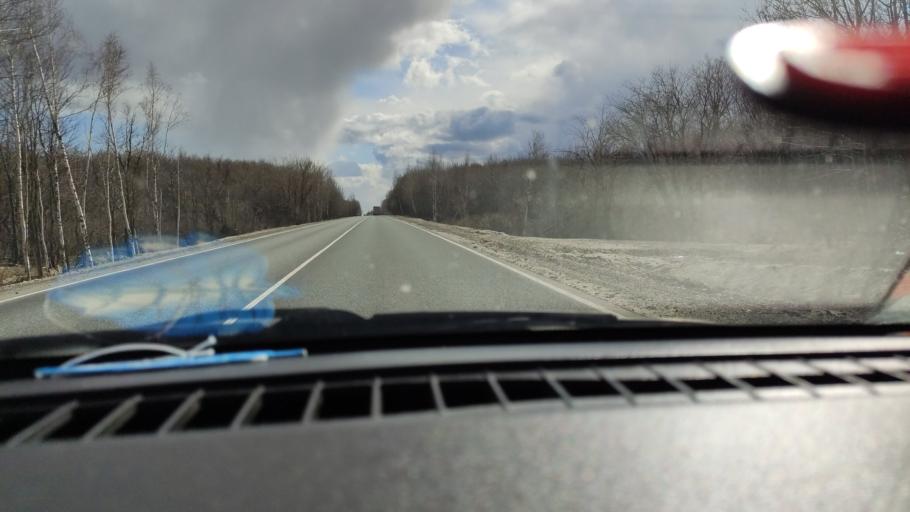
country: RU
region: Saratov
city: Khvalynsk
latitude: 52.4512
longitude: 48.0123
